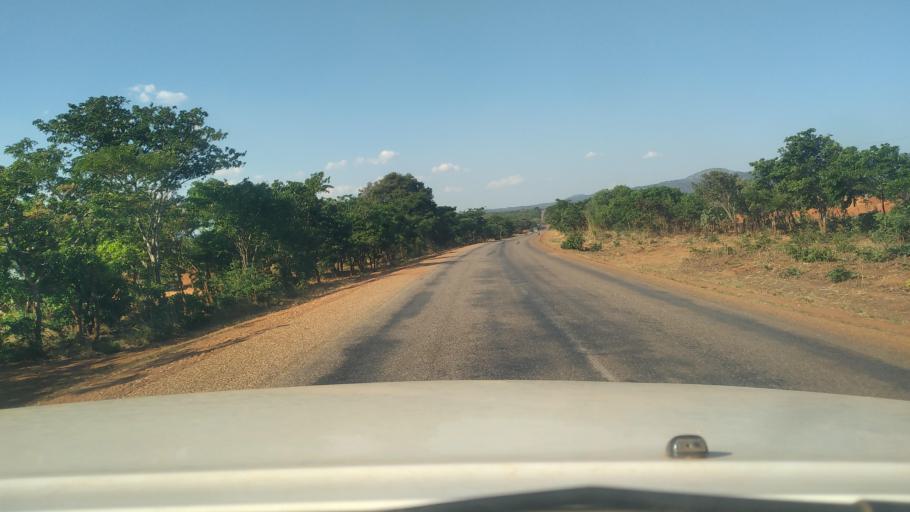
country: ZM
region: Northern
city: Mpika
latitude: -11.7488
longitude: 31.4649
